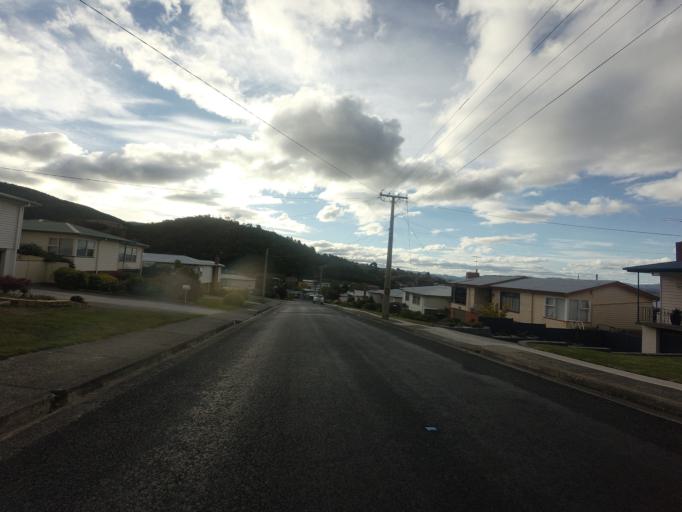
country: AU
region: Tasmania
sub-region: Glenorchy
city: Glenorchy
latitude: -42.8293
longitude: 147.2608
